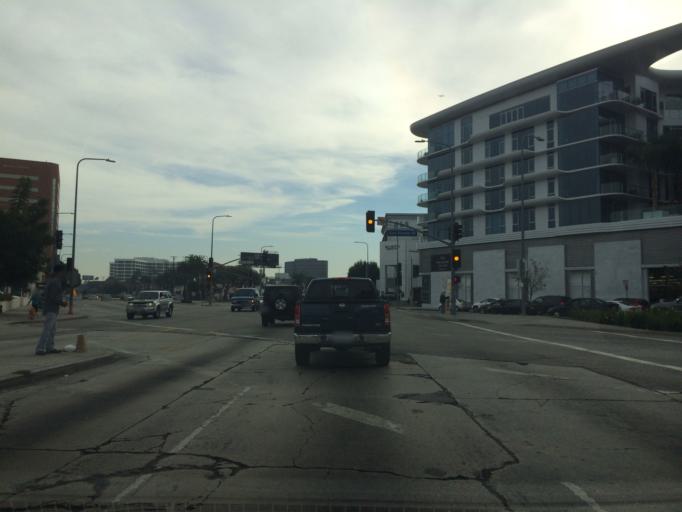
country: US
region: California
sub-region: Los Angeles County
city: West Hollywood
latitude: 34.0719
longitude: -118.3765
